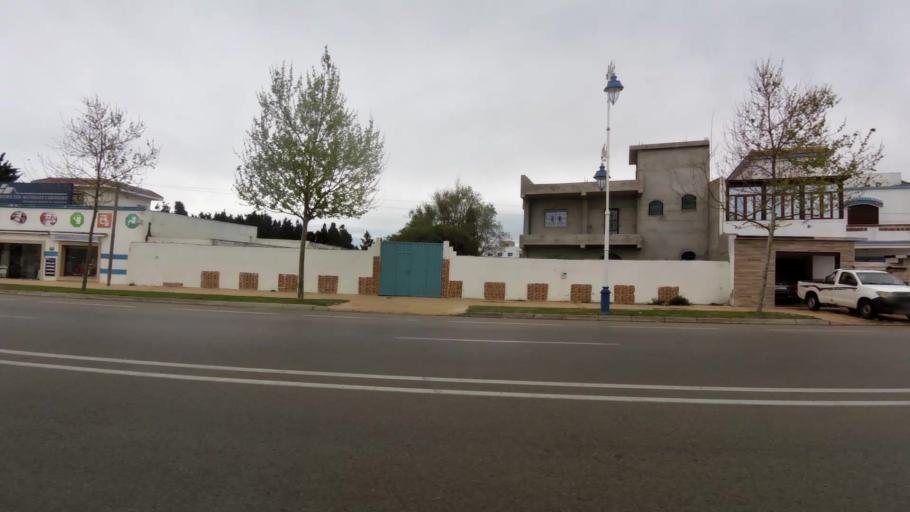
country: MA
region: Tanger-Tetouan
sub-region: Tetouan
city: Martil
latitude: 35.6370
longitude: -5.2899
